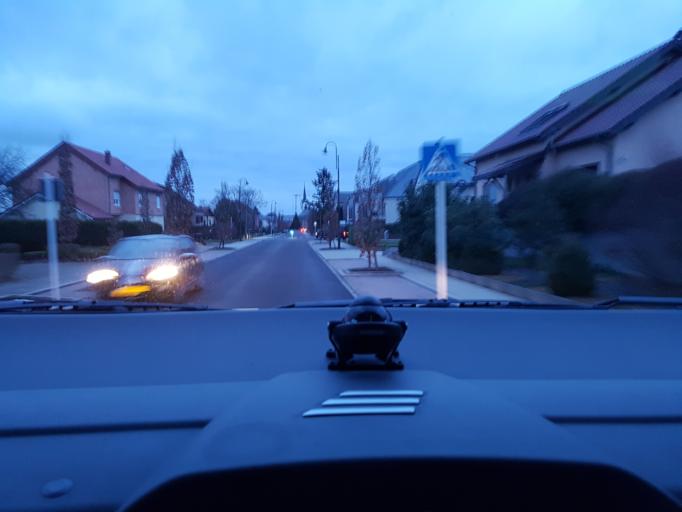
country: LU
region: Grevenmacher
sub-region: Canton de Remich
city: Mondorf-les-Bains
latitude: 49.5035
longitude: 6.3195
